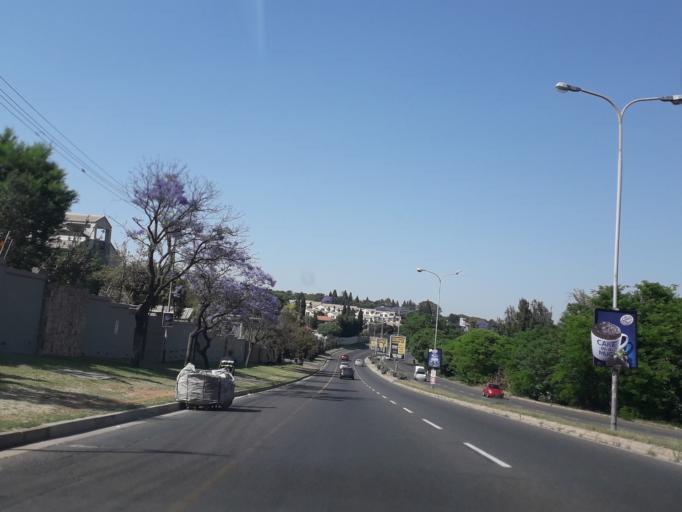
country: ZA
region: Gauteng
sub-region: City of Johannesburg Metropolitan Municipality
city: Diepsloot
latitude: -26.0634
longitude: 28.0207
